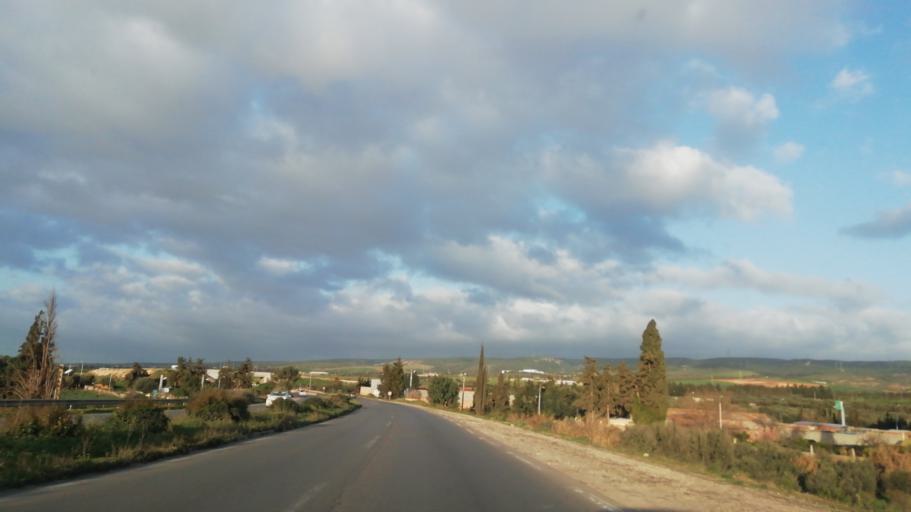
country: DZ
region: Oran
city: Mers el Kebir
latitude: 35.6077
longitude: -0.7454
